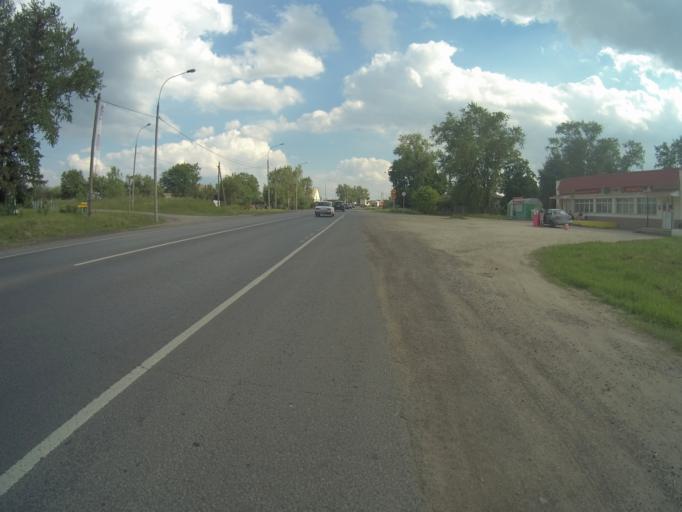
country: RU
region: Vladimir
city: Suzdal'
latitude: 56.3194
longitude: 40.4732
